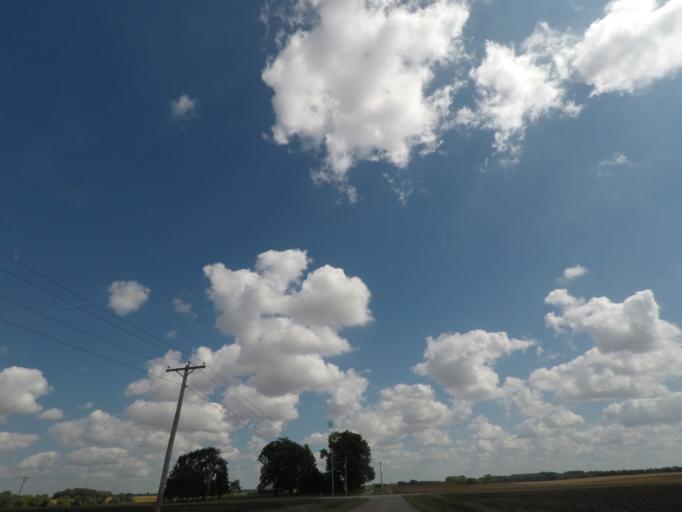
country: US
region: Iowa
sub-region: Story County
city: Nevada
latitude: 42.0706
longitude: -93.3877
